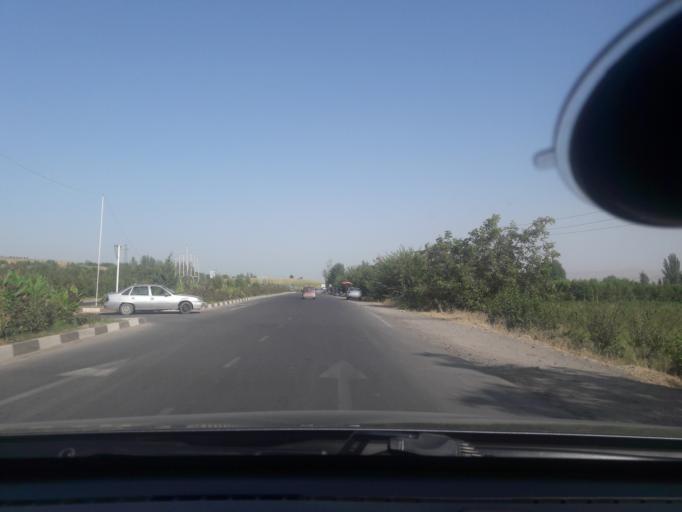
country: TJ
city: Shahrinav
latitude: 38.5739
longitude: 68.3626
